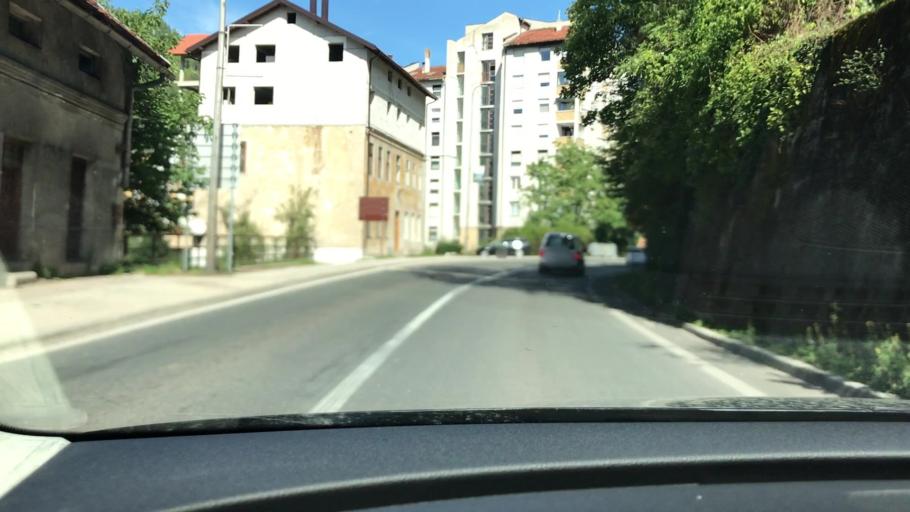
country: BA
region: Federation of Bosnia and Herzegovina
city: Konjic
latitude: 43.6559
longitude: 17.9640
